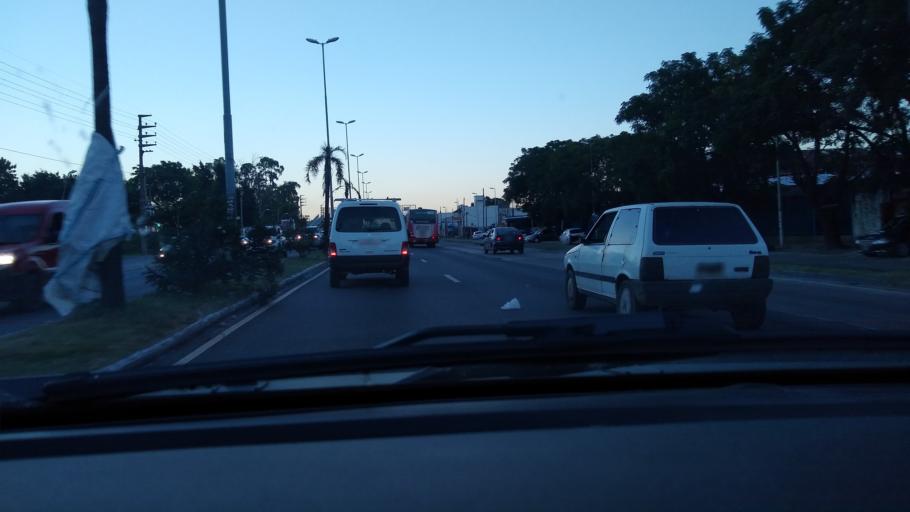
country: AR
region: Buenos Aires
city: San Justo
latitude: -34.6938
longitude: -58.5495
